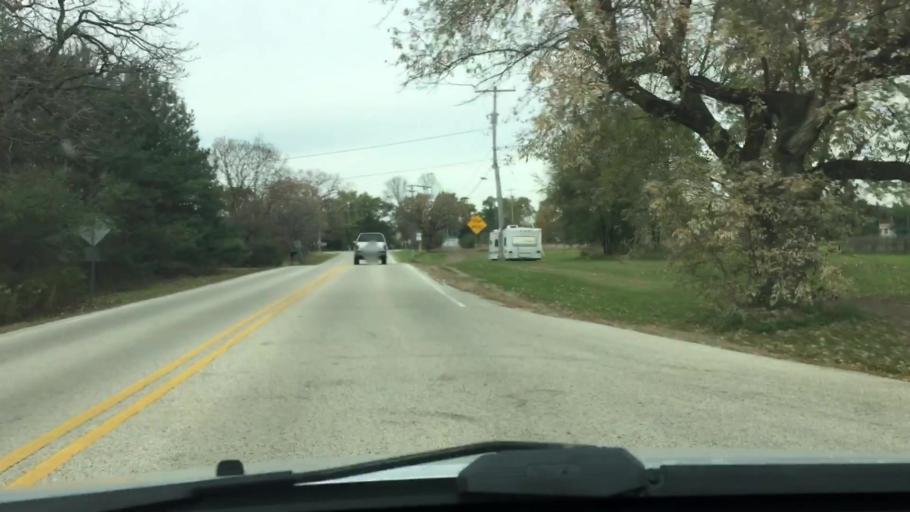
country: US
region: Wisconsin
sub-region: Waukesha County
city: North Prairie
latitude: 42.9065
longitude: -88.4068
